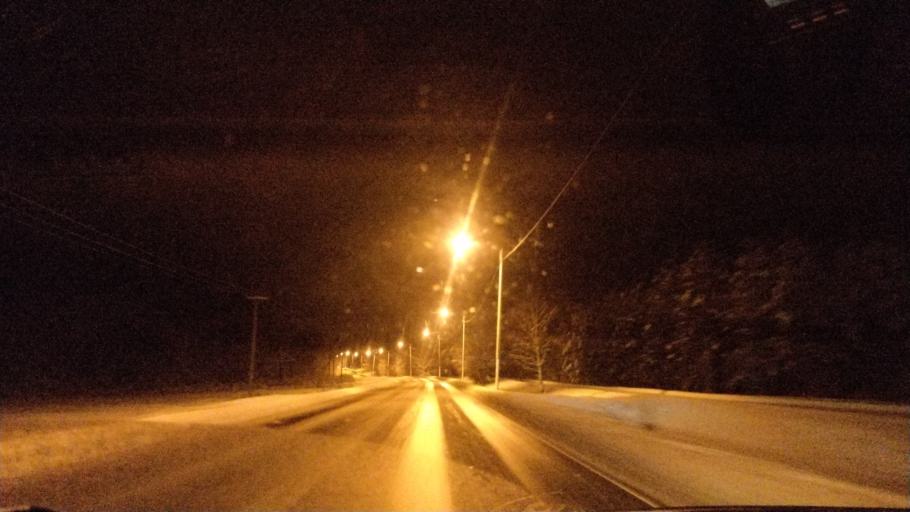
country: FI
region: Lapland
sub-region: Rovaniemi
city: Rovaniemi
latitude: 66.3029
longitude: 25.3552
